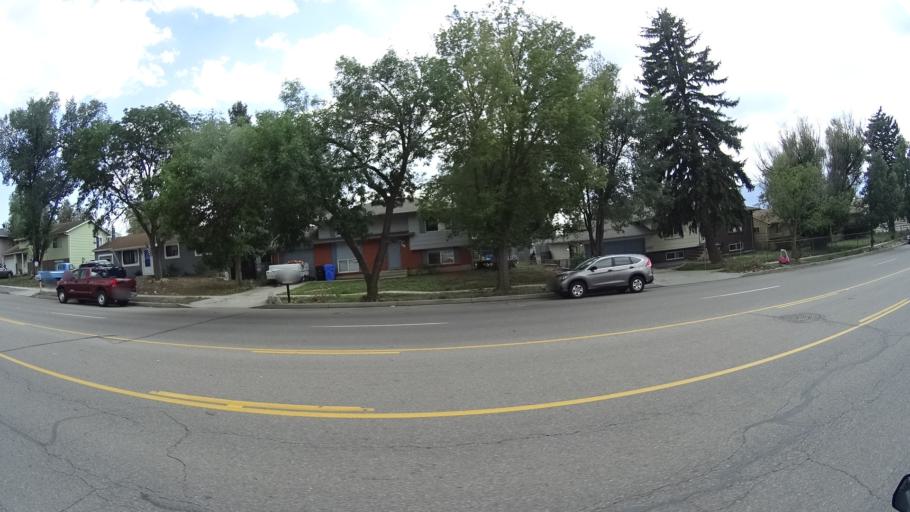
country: US
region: Colorado
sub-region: El Paso County
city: Cimarron Hills
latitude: 38.8320
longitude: -104.7544
